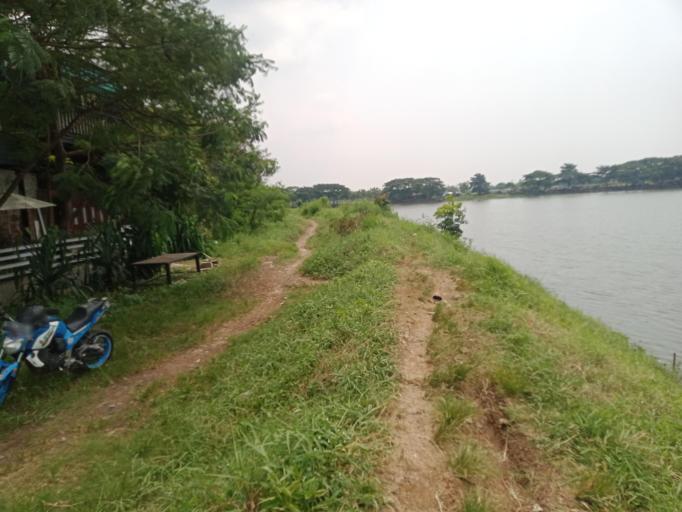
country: ID
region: Banten
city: Tangerang
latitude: -6.1642
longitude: 106.5904
